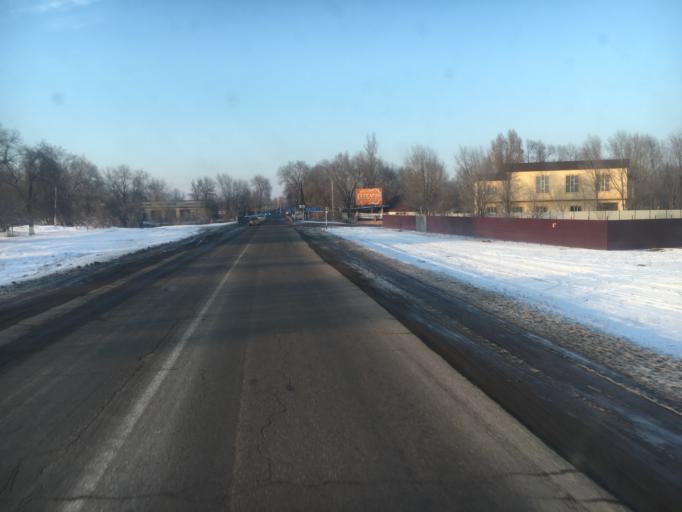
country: KZ
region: Almaty Oblysy
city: Burunday
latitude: 43.3652
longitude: 76.6418
